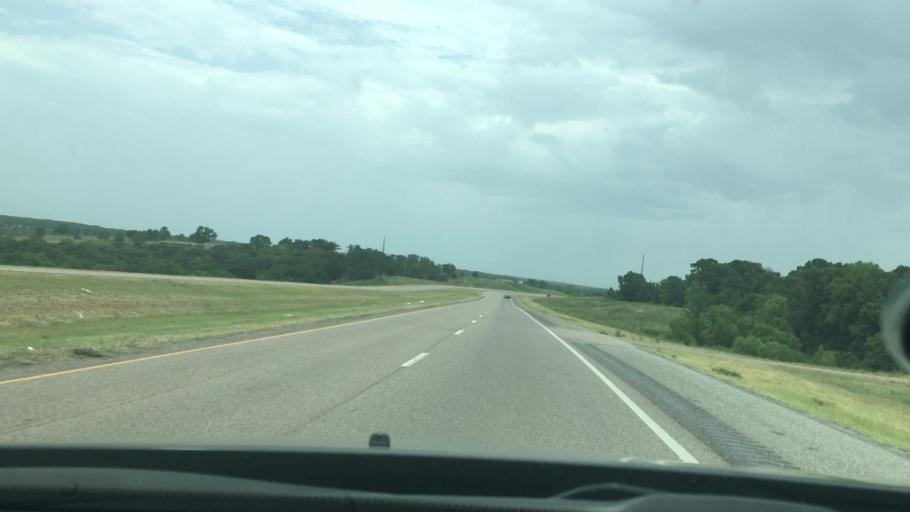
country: US
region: Oklahoma
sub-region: Pontotoc County
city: Ada
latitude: 34.8208
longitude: -96.6930
